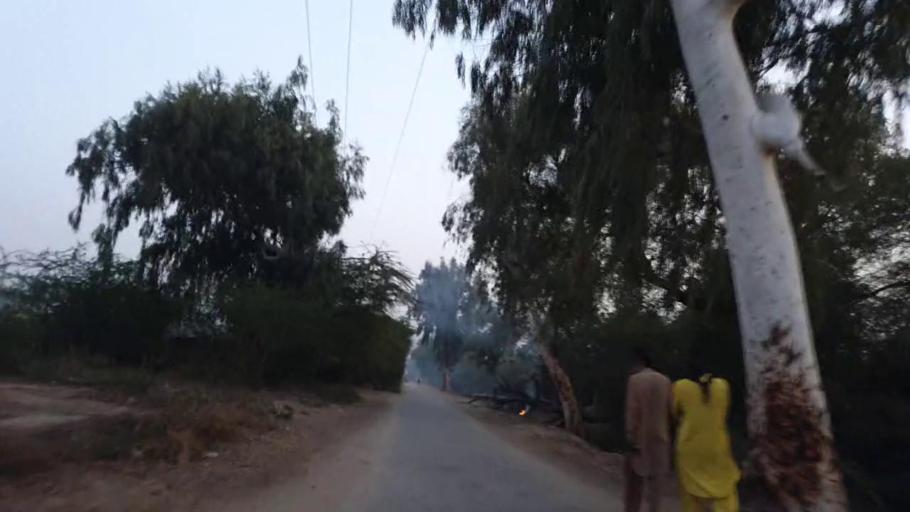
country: PK
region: Sindh
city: Tando Ghulam Ali
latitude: 25.1237
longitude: 68.8989
